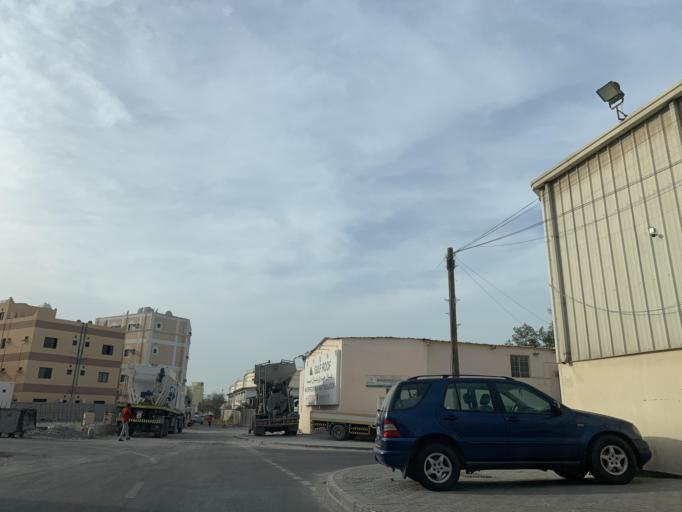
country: BH
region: Northern
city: Ar Rifa'
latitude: 26.1235
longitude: 50.5856
